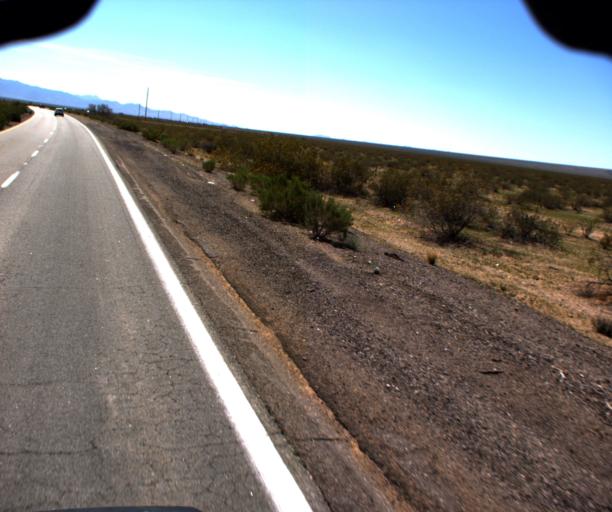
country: US
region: Arizona
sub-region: Mohave County
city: Dolan Springs
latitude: 35.6652
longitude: -114.4551
